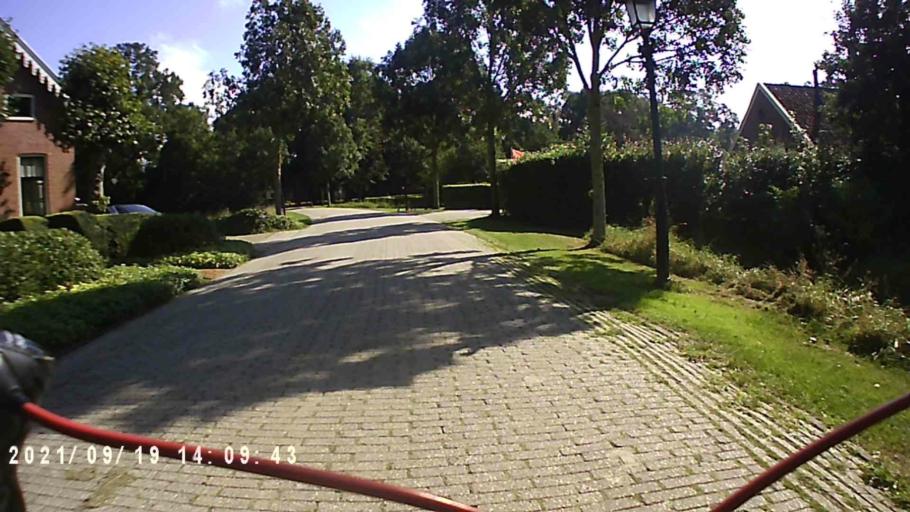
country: NL
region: Groningen
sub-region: Gemeente  Oldambt
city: Winschoten
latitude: 53.1386
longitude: 7.1383
